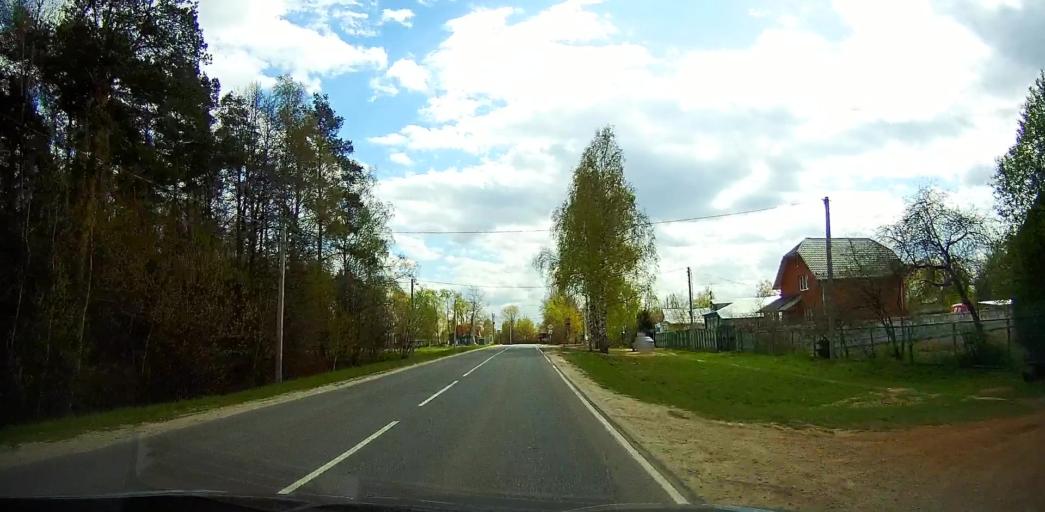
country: RU
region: Moskovskaya
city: Davydovo
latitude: 55.6495
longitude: 38.7551
